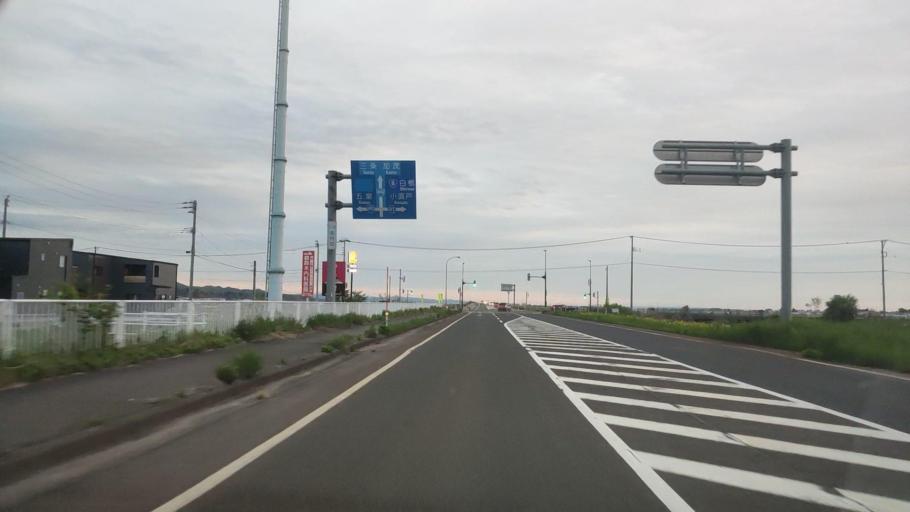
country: JP
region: Niigata
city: Niitsu-honcho
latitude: 37.7521
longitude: 139.0885
